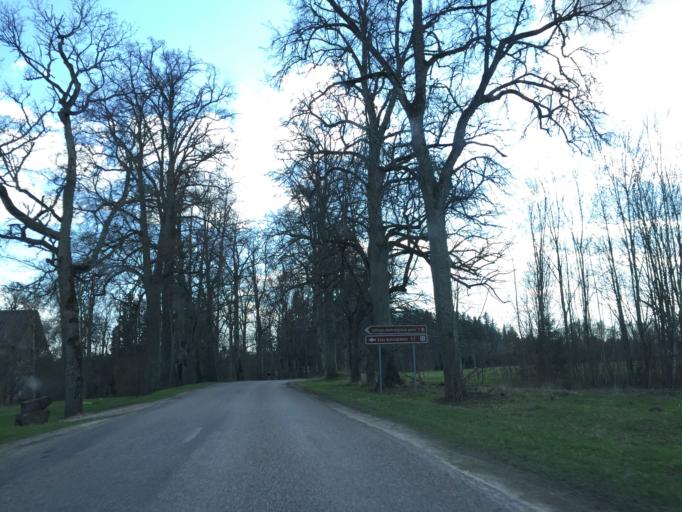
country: LV
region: Krimulda
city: Ragana
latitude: 57.3426
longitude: 24.6569
